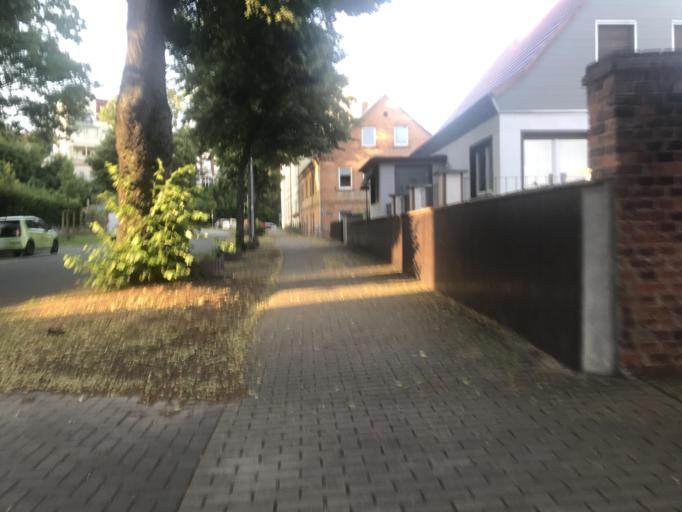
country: DE
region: Saxony-Anhalt
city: Quedlinburg
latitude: 51.7951
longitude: 11.1455
